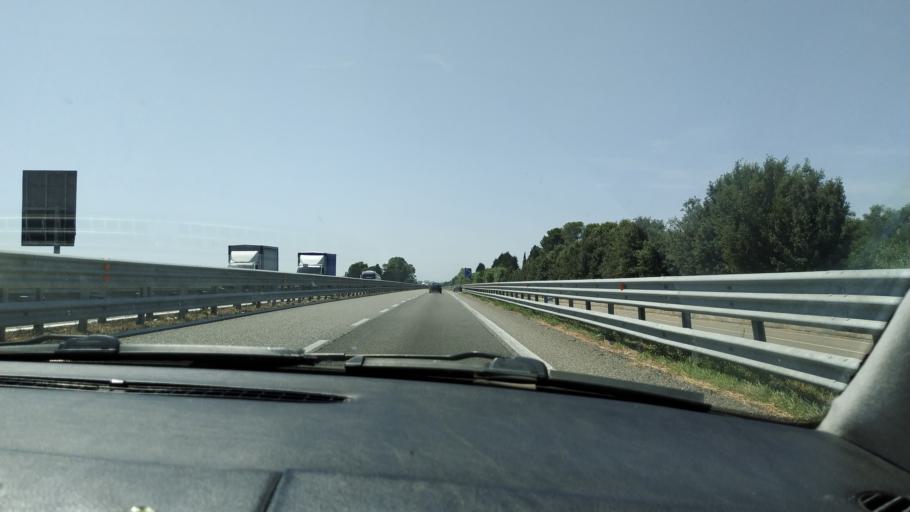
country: IT
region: Basilicate
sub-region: Provincia di Matera
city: Marconia
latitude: 40.3581
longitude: 16.7764
